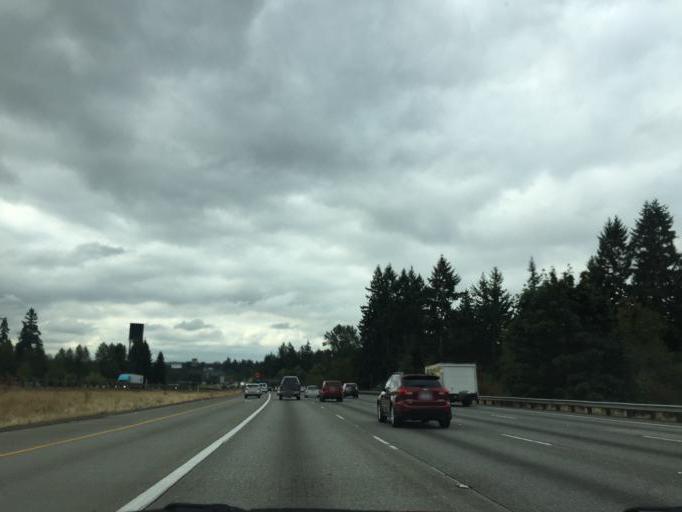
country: US
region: Washington
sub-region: Pierce County
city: Fife Heights
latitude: 47.2609
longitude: -122.3271
